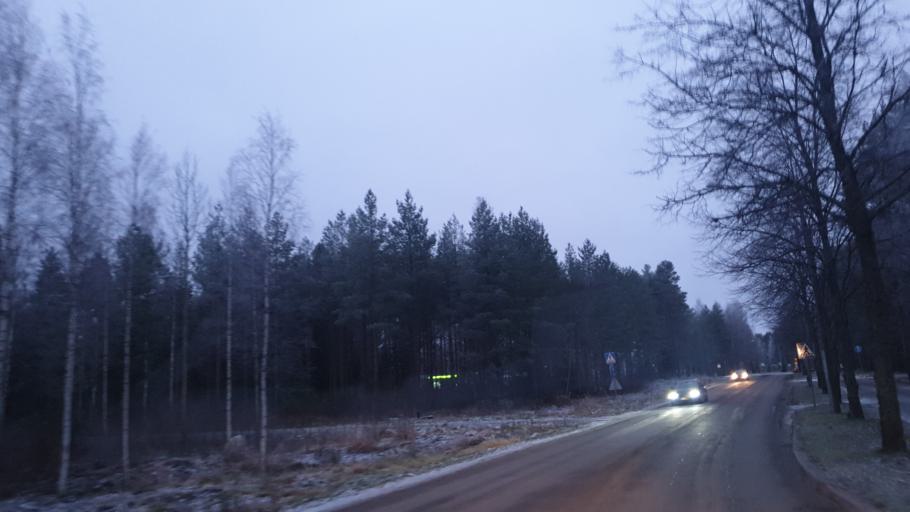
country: FI
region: Southern Ostrobothnia
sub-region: Seinaejoki
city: Seinaejoki
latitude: 62.7732
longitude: 22.8771
